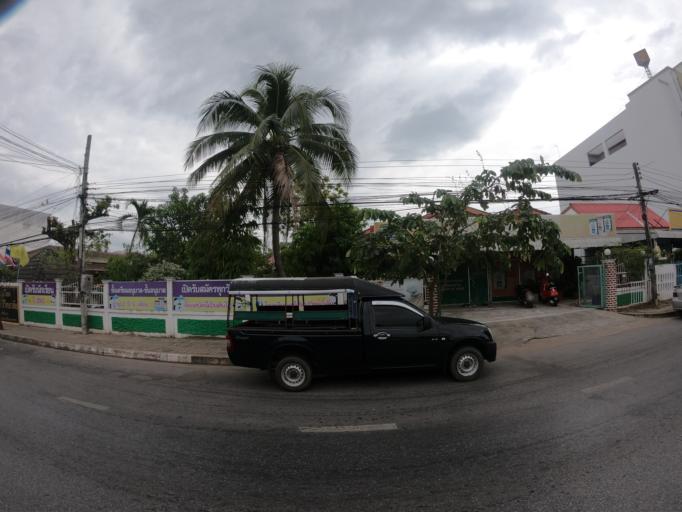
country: TH
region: Roi Et
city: Roi Et
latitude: 16.0533
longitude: 103.6473
